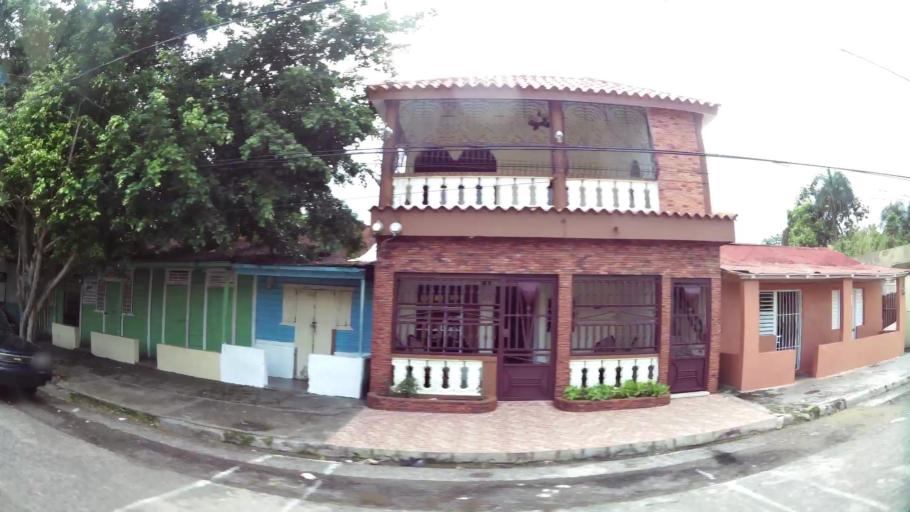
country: DO
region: San Cristobal
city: Villa Altagracia
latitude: 18.6724
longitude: -70.1758
